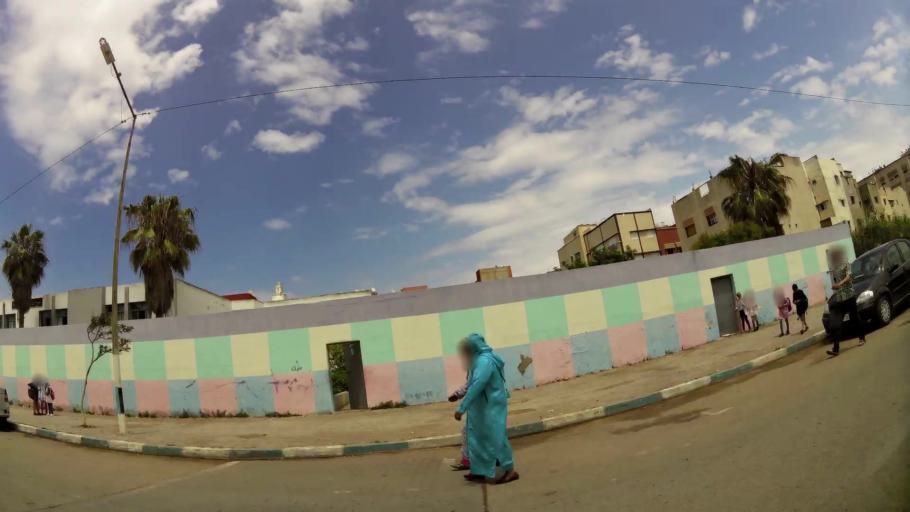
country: MA
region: Rabat-Sale-Zemmour-Zaer
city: Sale
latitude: 34.0531
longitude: -6.8173
